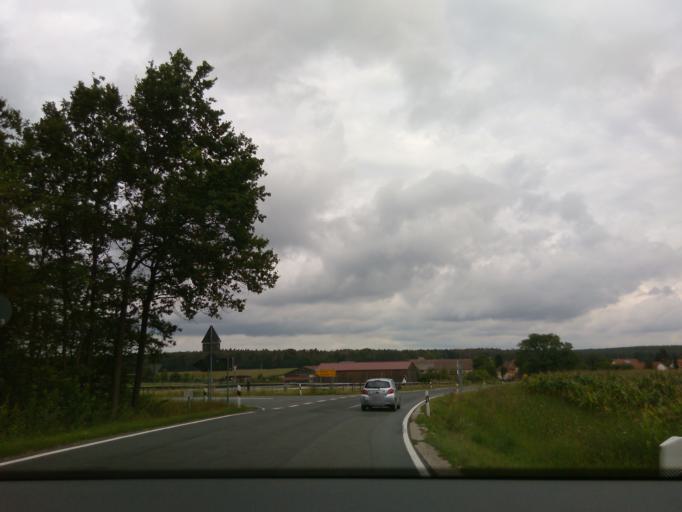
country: DE
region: Bavaria
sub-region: Regierungsbezirk Mittelfranken
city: Weisendorf
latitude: 49.6538
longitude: 10.8086
